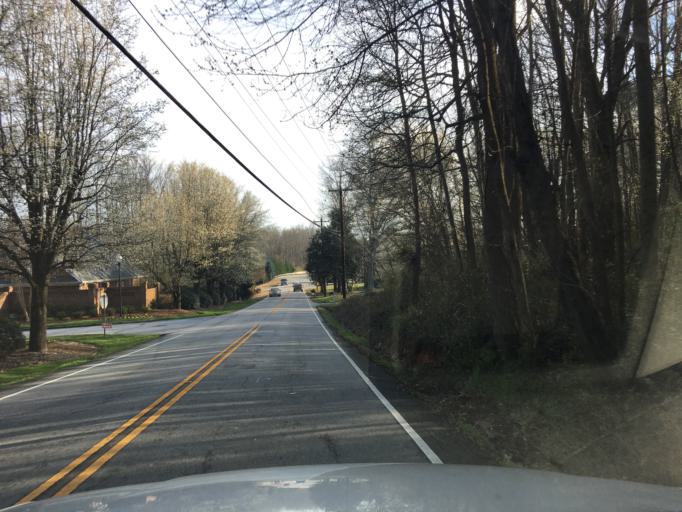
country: US
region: South Carolina
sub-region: Greenville County
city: Taylors
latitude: 34.8863
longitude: -82.2903
